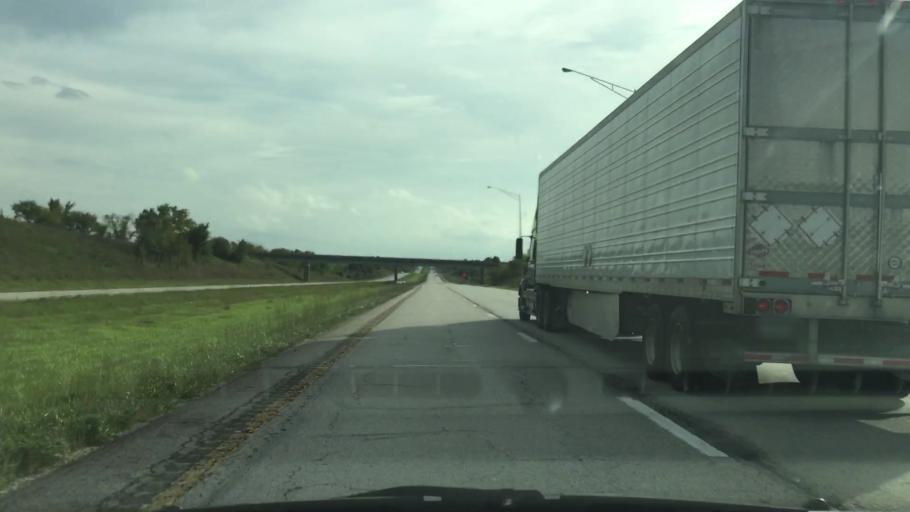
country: US
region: Iowa
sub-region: Decatur County
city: Lamoni
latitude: 40.5466
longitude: -93.9545
